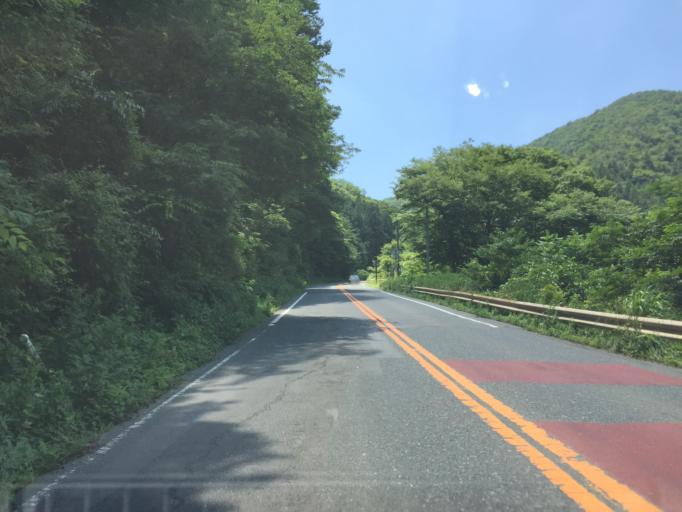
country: JP
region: Miyagi
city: Marumori
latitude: 37.7764
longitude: 140.8005
